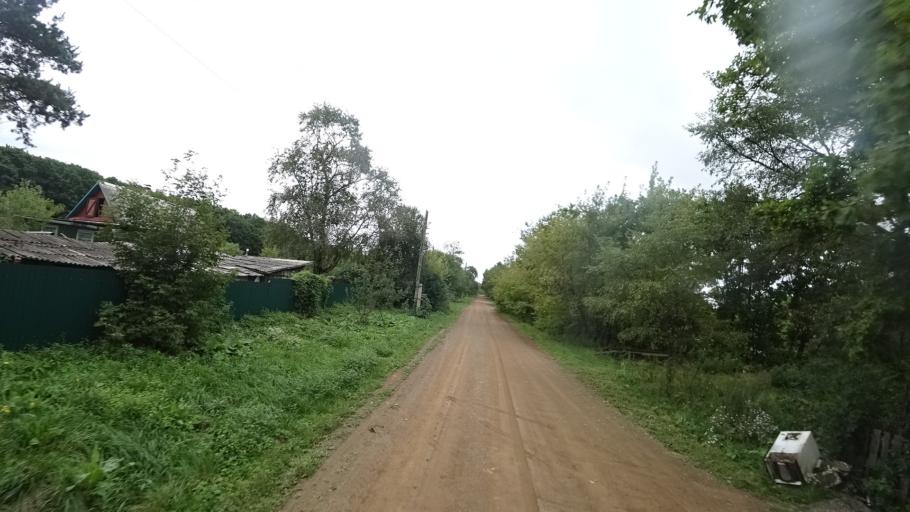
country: RU
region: Primorskiy
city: Chernigovka
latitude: 44.4410
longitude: 132.5739
